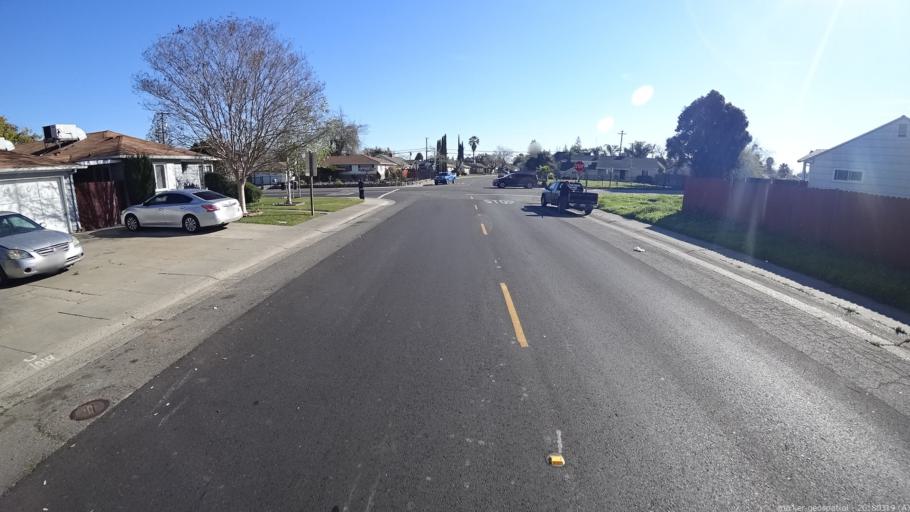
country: US
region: California
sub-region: Sacramento County
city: Parkway
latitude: 38.4937
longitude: -121.4495
